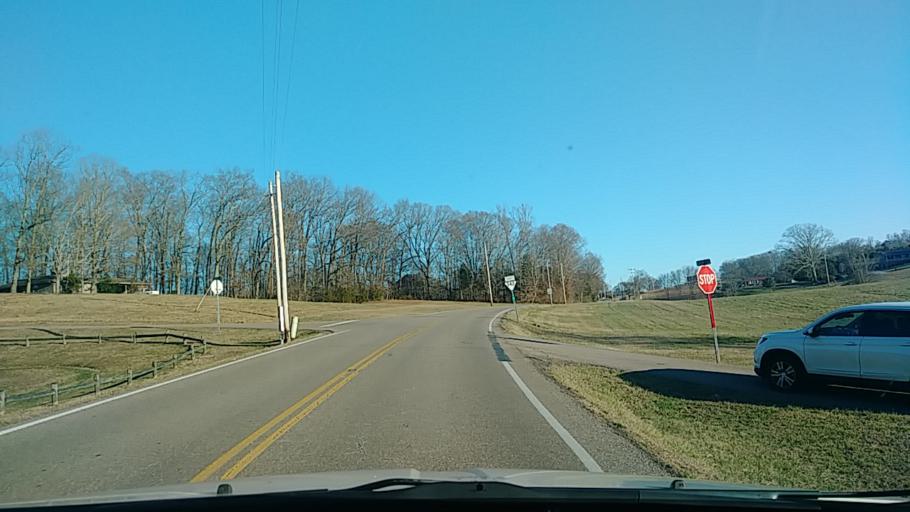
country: US
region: Tennessee
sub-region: Hamblen County
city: Morristown
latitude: 36.2052
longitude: -83.4069
